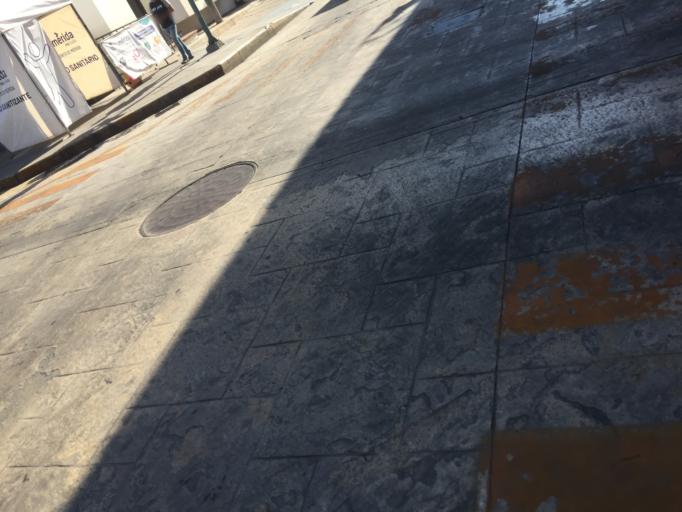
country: MX
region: Yucatan
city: Merida
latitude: 20.9682
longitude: -89.6205
